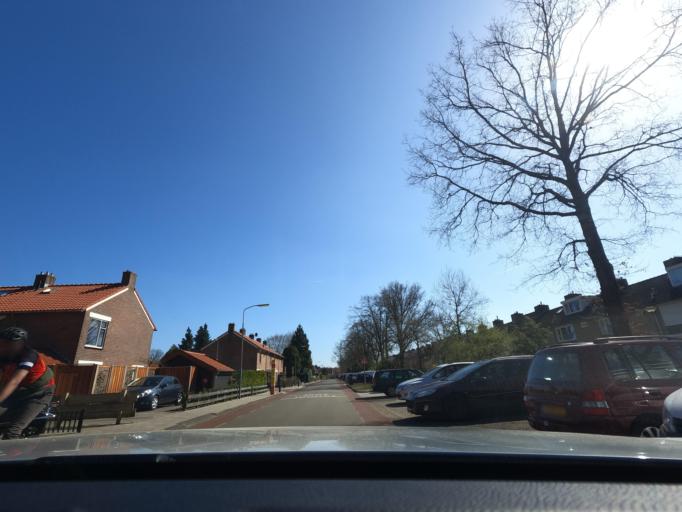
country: NL
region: Gelderland
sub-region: Gemeente Oldebroek
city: Oldebroek
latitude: 52.4161
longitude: 5.8757
